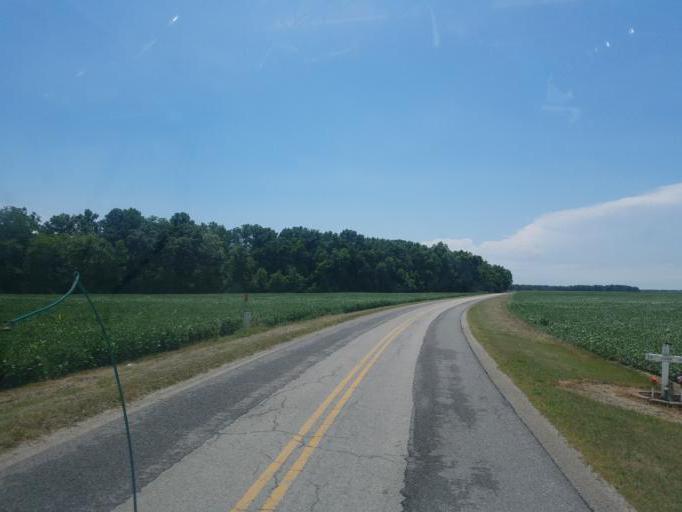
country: US
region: Ohio
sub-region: Paulding County
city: Antwerp
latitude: 41.1909
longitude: -84.7671
